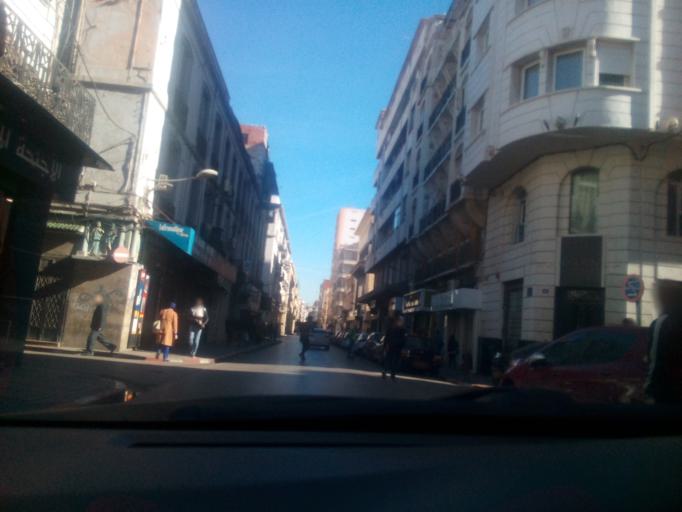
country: DZ
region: Oran
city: Oran
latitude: 35.7022
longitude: -0.6421
